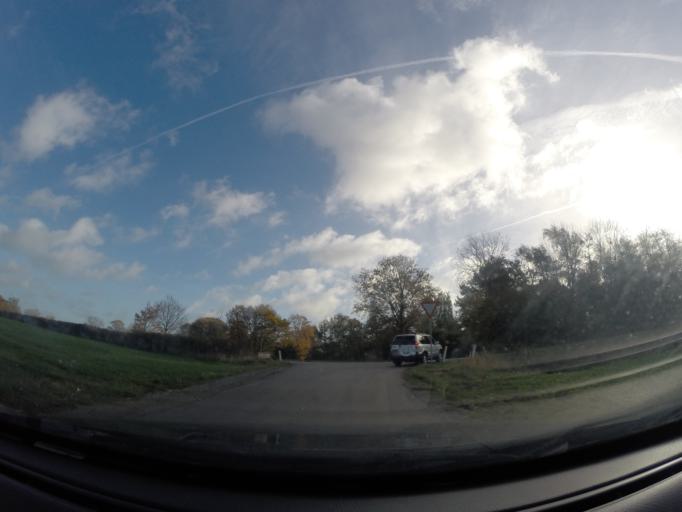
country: DK
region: South Denmark
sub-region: Faaborg-Midtfyn Kommune
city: Ringe
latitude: 55.2048
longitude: 10.5637
